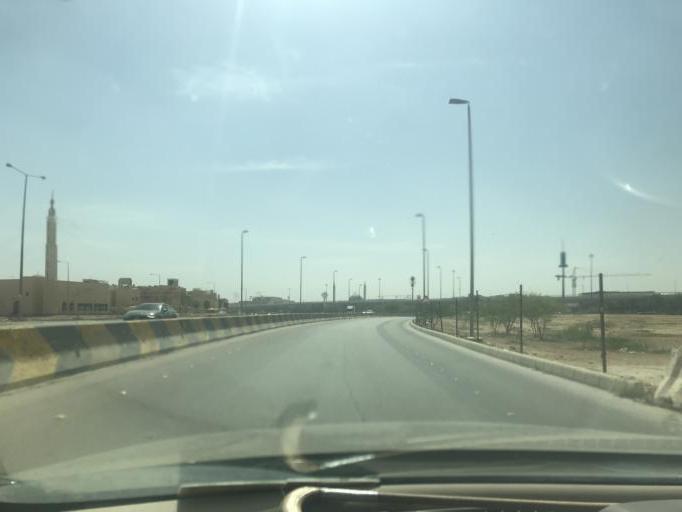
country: SA
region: Ar Riyad
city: Riyadh
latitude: 24.8229
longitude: 46.7199
